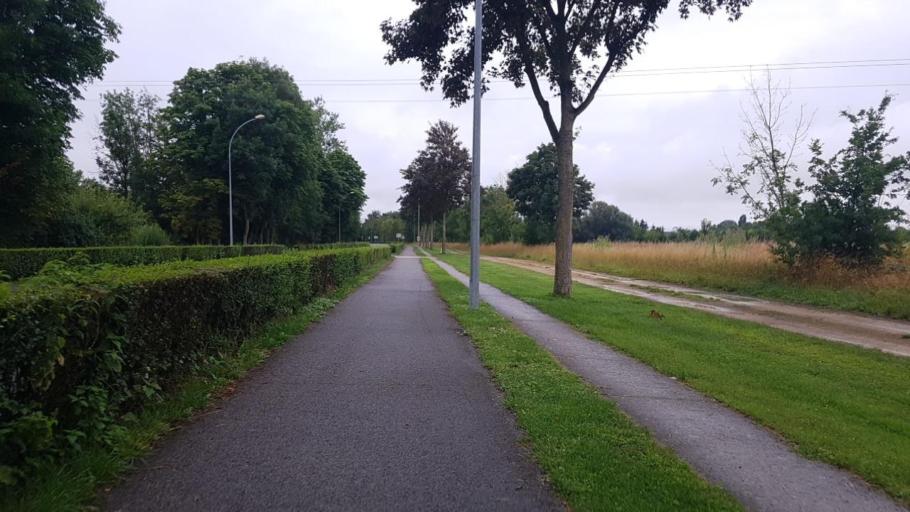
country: FR
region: Champagne-Ardenne
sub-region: Departement de la Marne
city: Sarry
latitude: 48.9315
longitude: 4.3917
